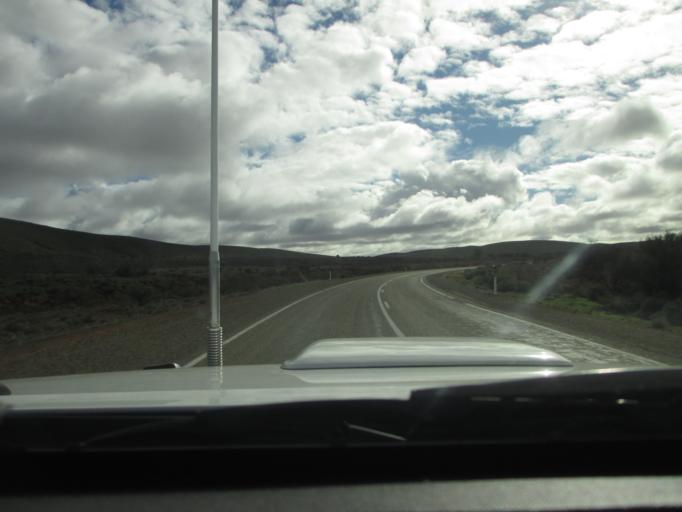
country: AU
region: South Australia
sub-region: Flinders Ranges
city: Quorn
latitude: -32.2135
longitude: 138.5193
